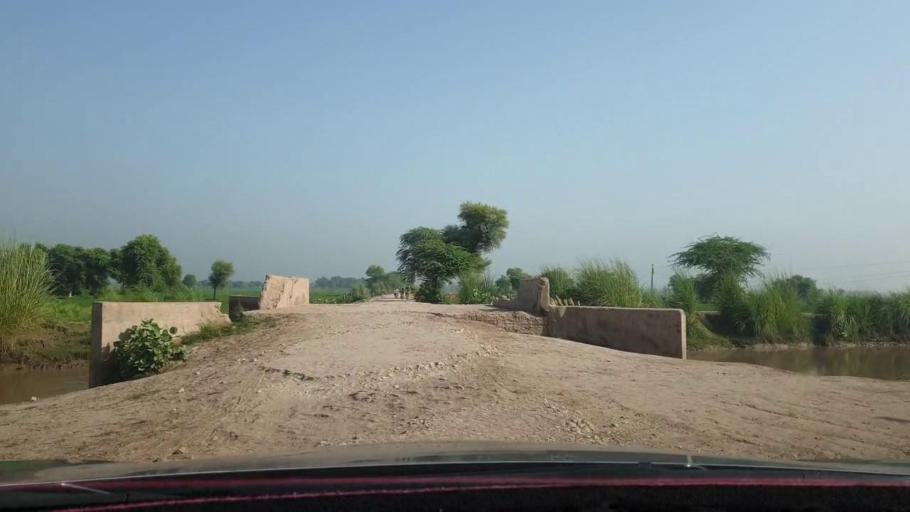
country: PK
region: Sindh
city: Nasirabad
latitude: 27.4339
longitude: 67.9204
